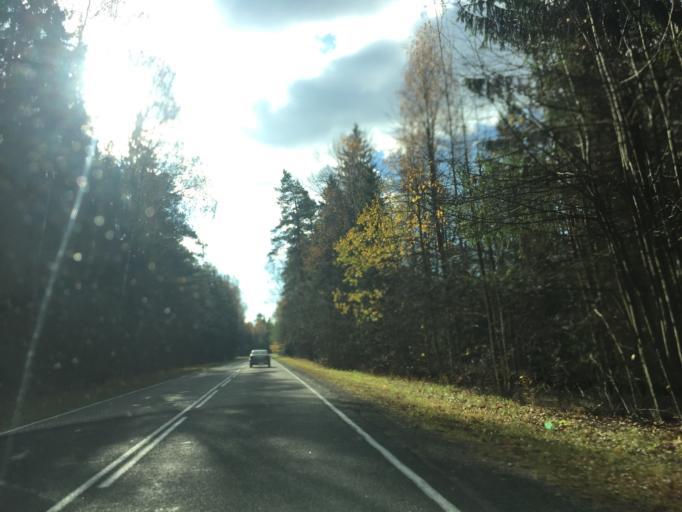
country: BY
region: Minsk
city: Narach
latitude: 54.9371
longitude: 26.5645
